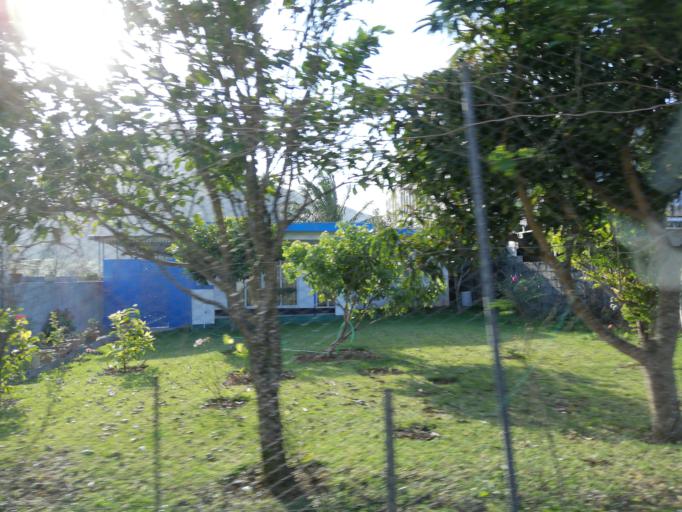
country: MU
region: Moka
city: Saint Pierre
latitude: -20.2154
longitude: 57.5244
